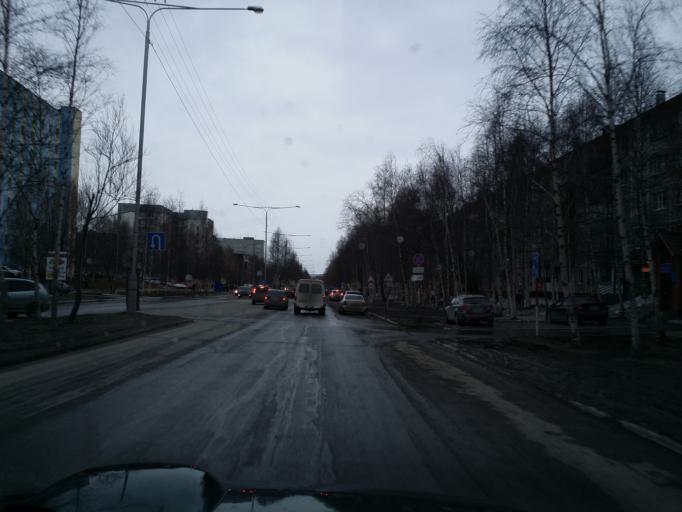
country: RU
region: Khanty-Mansiyskiy Avtonomnyy Okrug
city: Nizhnevartovsk
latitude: 60.9445
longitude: 76.5662
